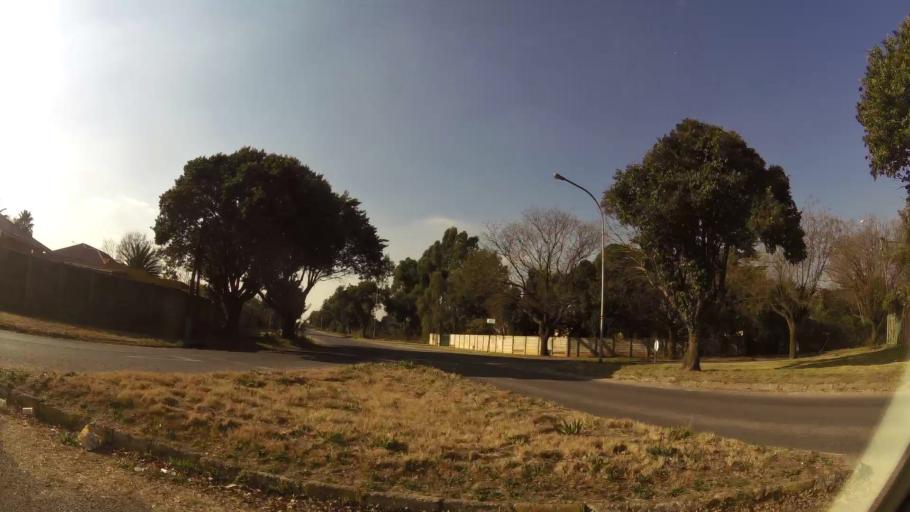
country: ZA
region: Gauteng
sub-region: Ekurhuleni Metropolitan Municipality
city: Brakpan
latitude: -26.2217
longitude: 28.3617
